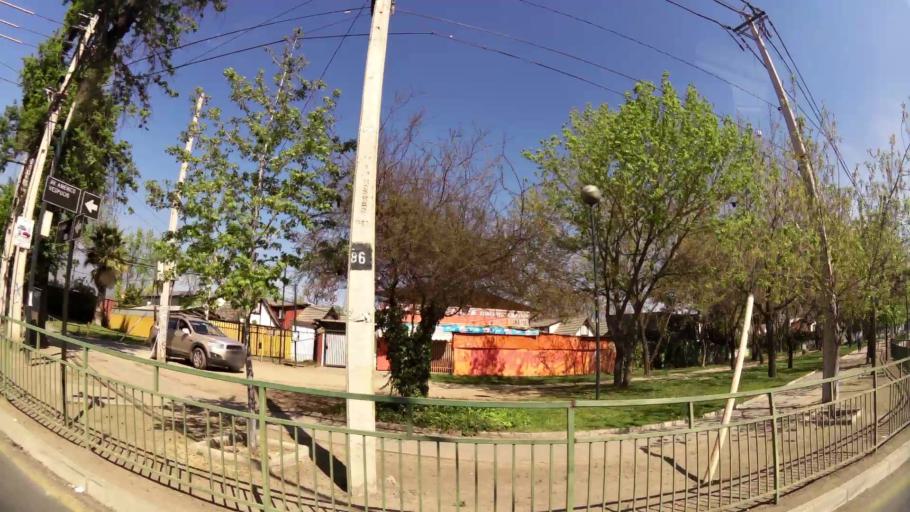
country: CL
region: Santiago Metropolitan
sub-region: Provincia de Santiago
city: Villa Presidente Frei, Nunoa, Santiago, Chile
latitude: -33.4898
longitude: -70.5794
